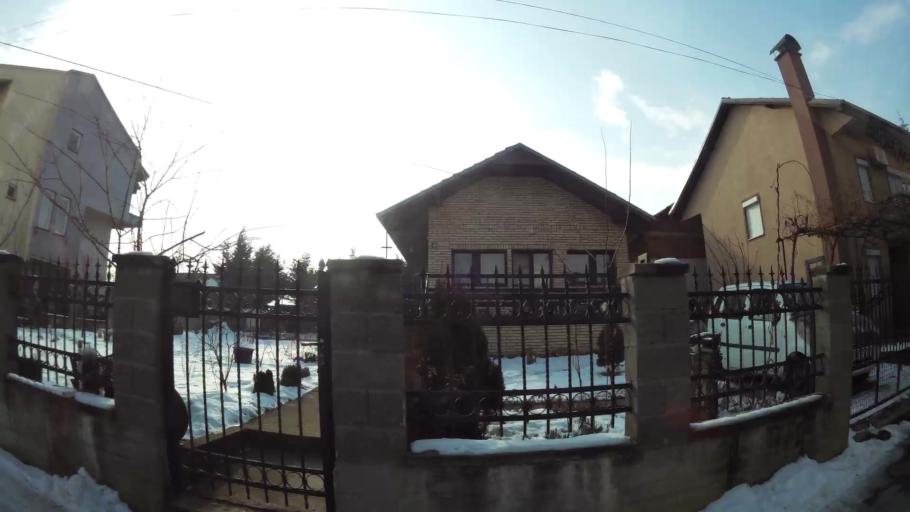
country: MK
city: Creshevo
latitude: 42.0092
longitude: 21.4976
